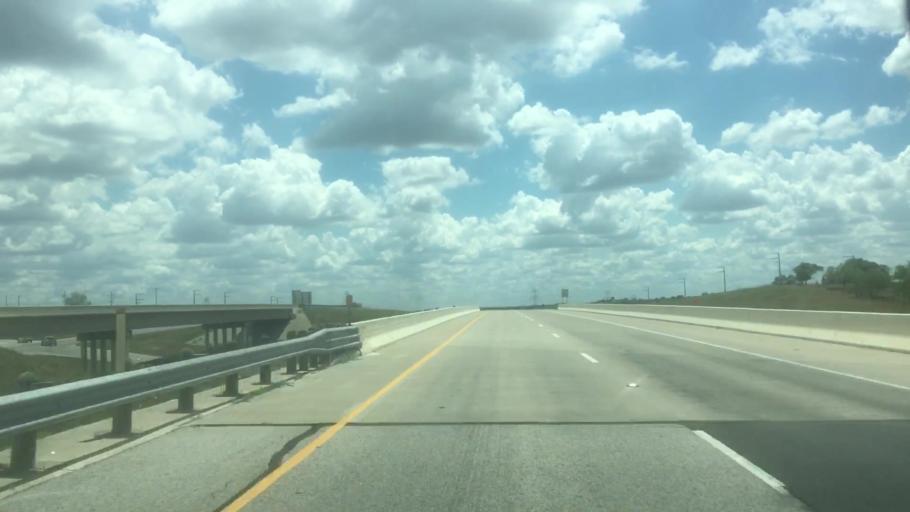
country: US
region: Texas
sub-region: Caldwell County
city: Uhland
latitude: 30.0060
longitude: -97.6875
